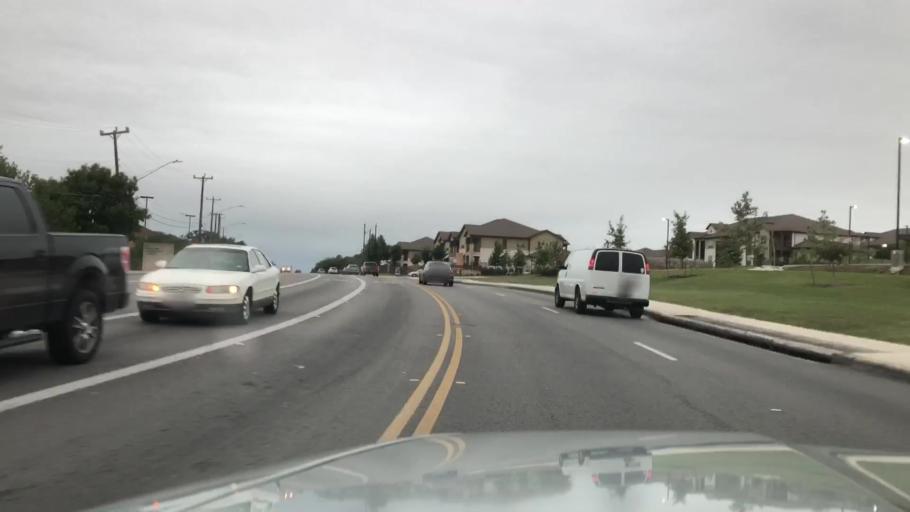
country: US
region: Texas
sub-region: Bexar County
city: Leon Valley
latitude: 29.5191
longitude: -98.6049
